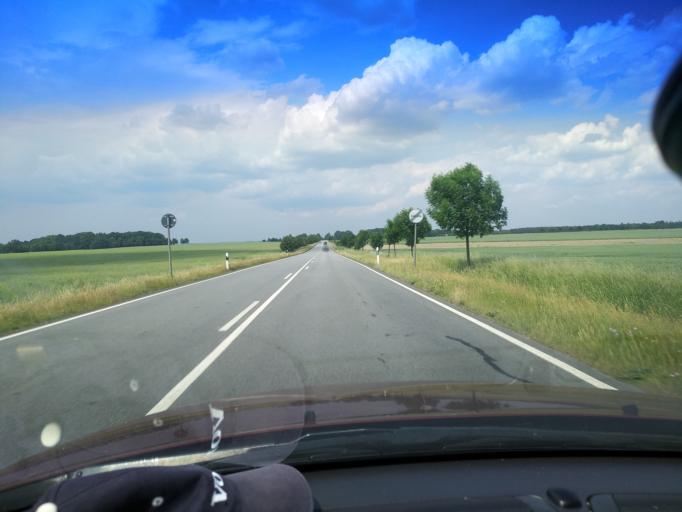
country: DE
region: Saxony
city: Kodersdorf
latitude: 51.2577
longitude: 14.8689
